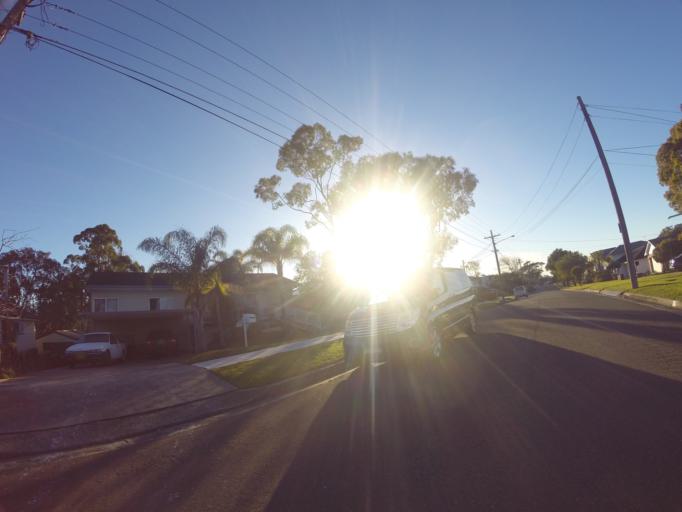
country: AU
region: New South Wales
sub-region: Sutherland Shire
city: Grays Point
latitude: -34.0602
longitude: 151.0760
